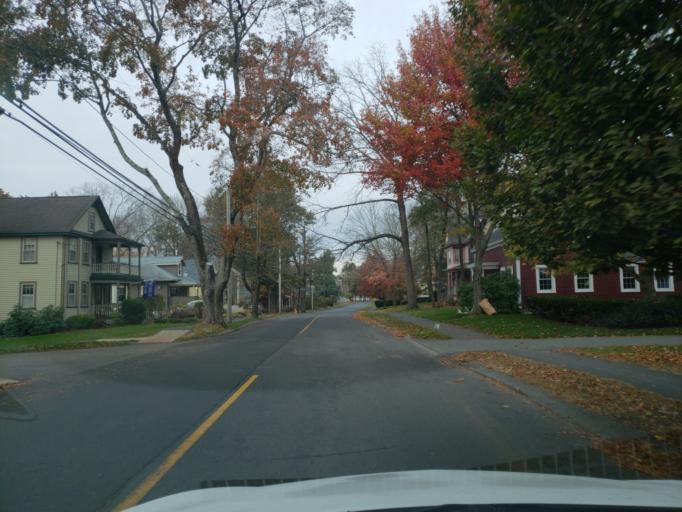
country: US
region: Massachusetts
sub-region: Essex County
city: Andover
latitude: 42.6590
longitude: -71.1329
